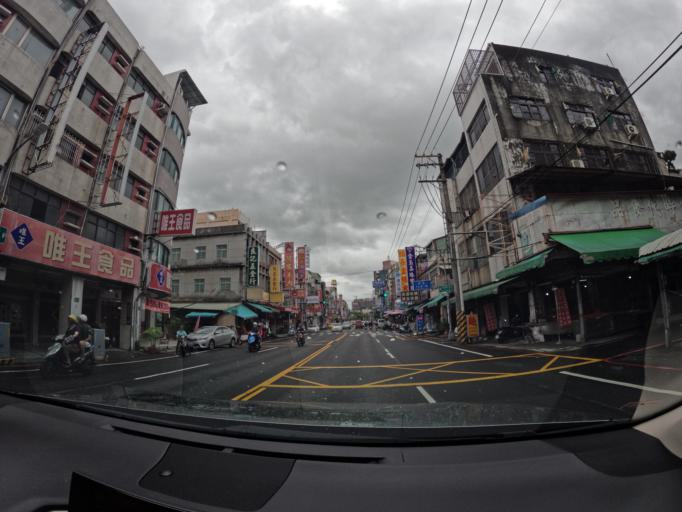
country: TW
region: Taiwan
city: Fengshan
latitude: 22.6257
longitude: 120.3603
